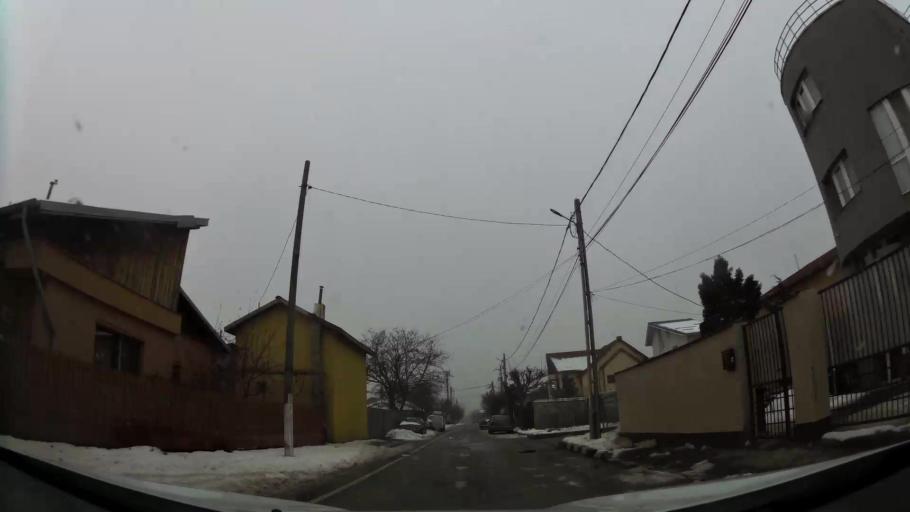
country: RO
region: Ilfov
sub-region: Comuna Chiajna
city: Rosu
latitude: 44.4549
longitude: 26.0058
